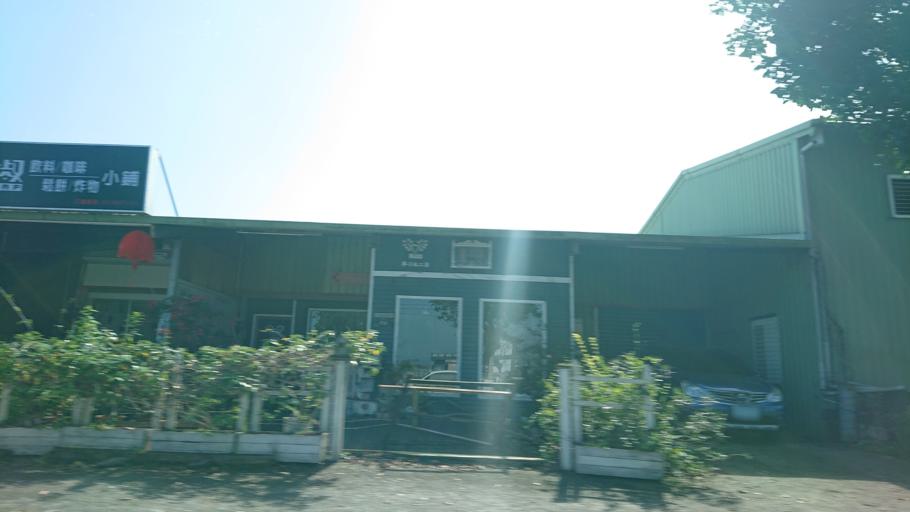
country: TW
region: Taiwan
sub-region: Yilan
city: Yilan
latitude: 24.6700
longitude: 121.7173
